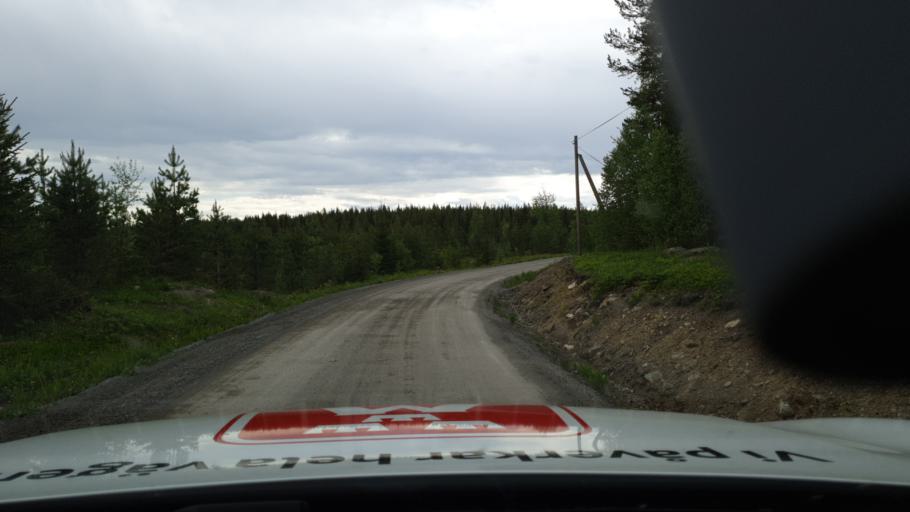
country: SE
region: Jaemtland
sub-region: OEstersunds Kommun
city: Brunflo
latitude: 62.9820
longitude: 14.7072
